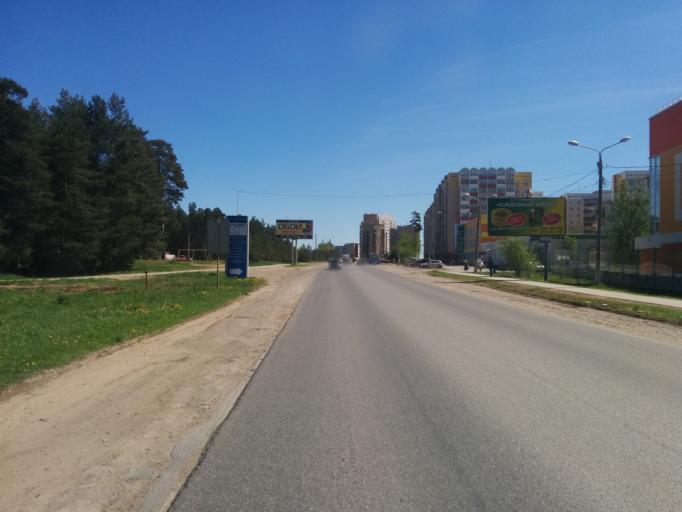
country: RU
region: Perm
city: Kondratovo
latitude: 58.0386
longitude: 56.1353
